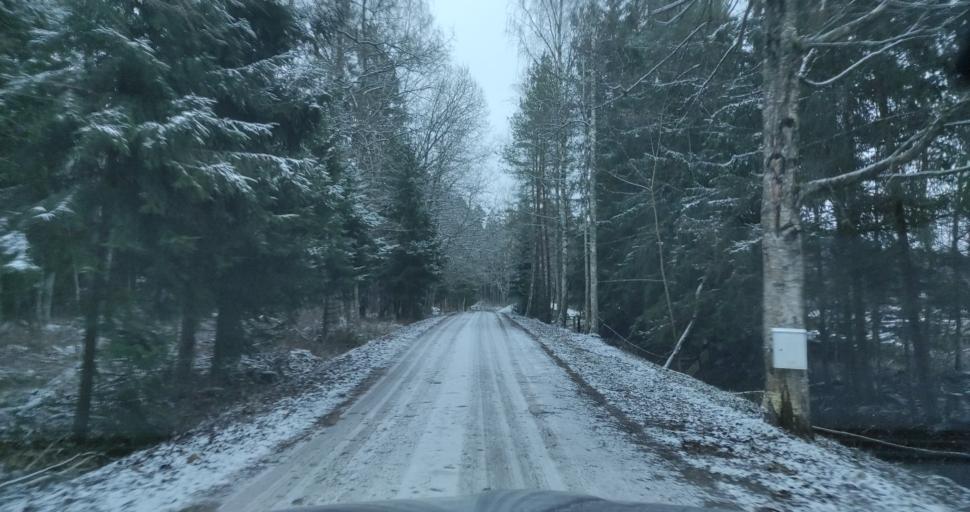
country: LV
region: Kuldigas Rajons
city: Kuldiga
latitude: 56.9788
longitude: 22.0309
